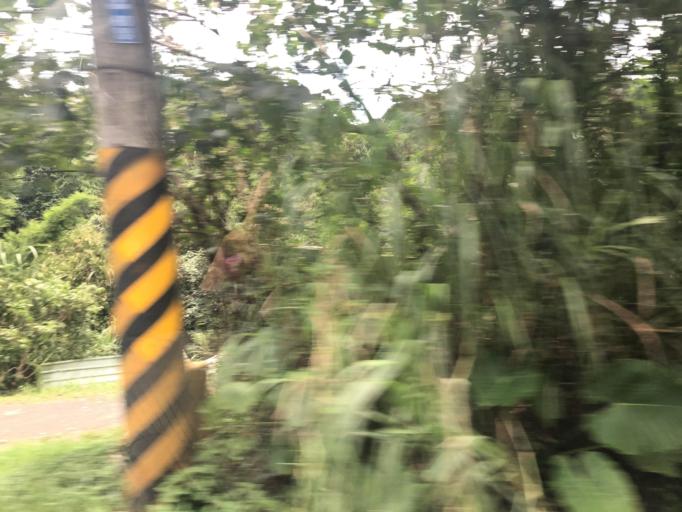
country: TW
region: Taipei
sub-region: Taipei
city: Banqiao
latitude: 24.9156
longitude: 121.4114
